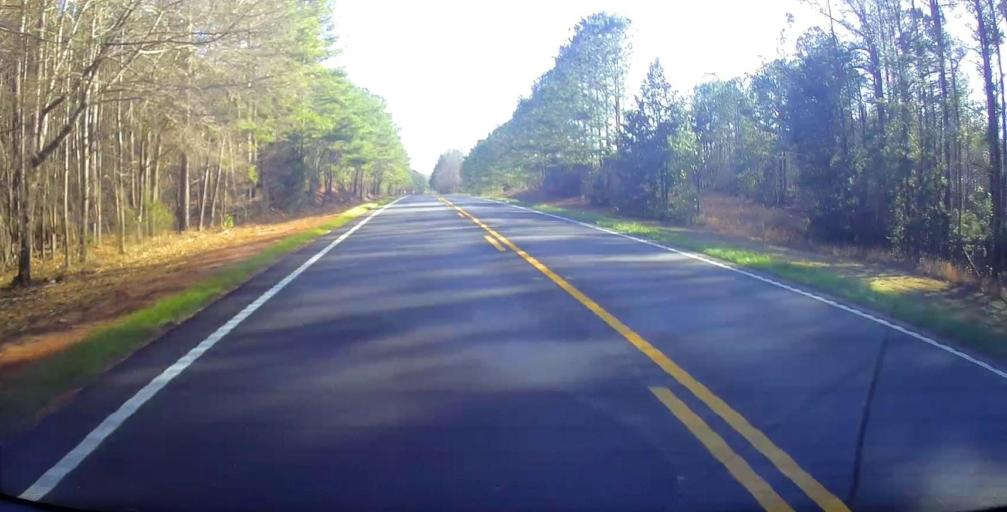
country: US
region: Georgia
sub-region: Talbot County
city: Sardis
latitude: 32.7844
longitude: -84.6927
